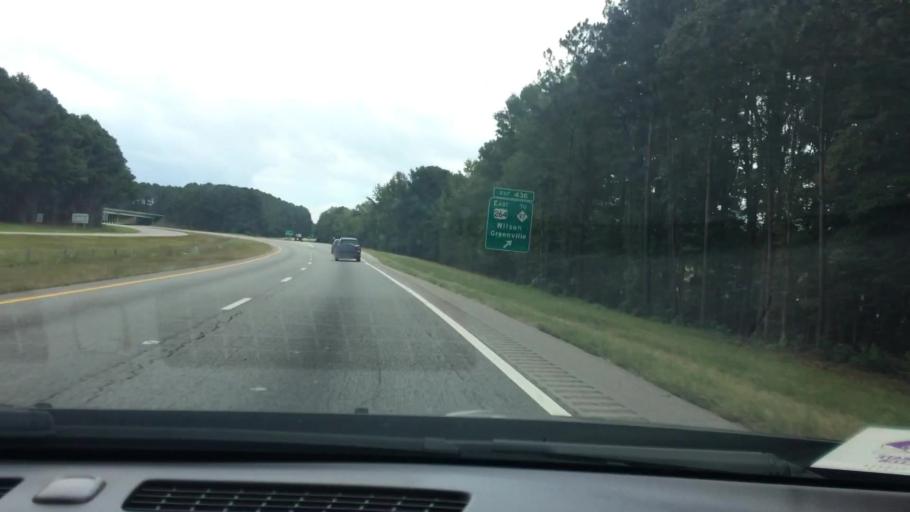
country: US
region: North Carolina
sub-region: Wake County
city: Zebulon
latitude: 35.8338
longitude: -78.3091
